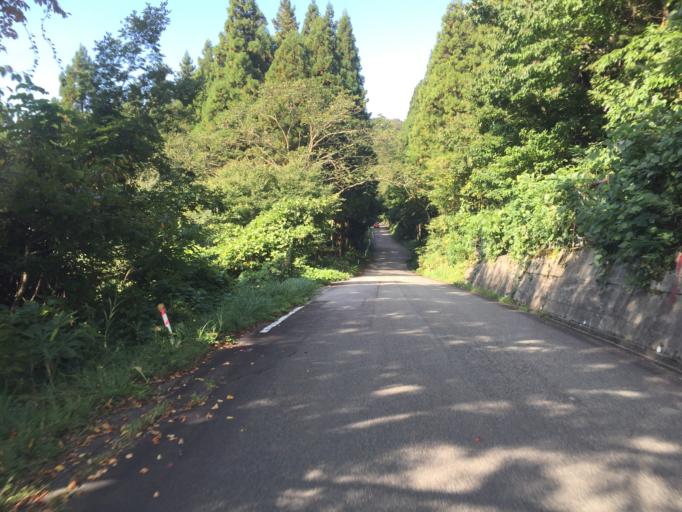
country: JP
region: Fukushima
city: Inawashiro
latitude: 37.4841
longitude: 139.9724
